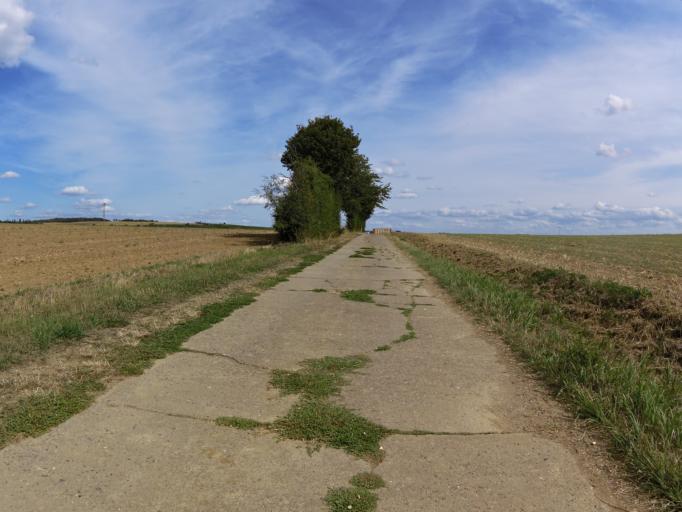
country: DE
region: Bavaria
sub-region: Regierungsbezirk Unterfranken
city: Rimpar
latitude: 49.8556
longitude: 9.9341
